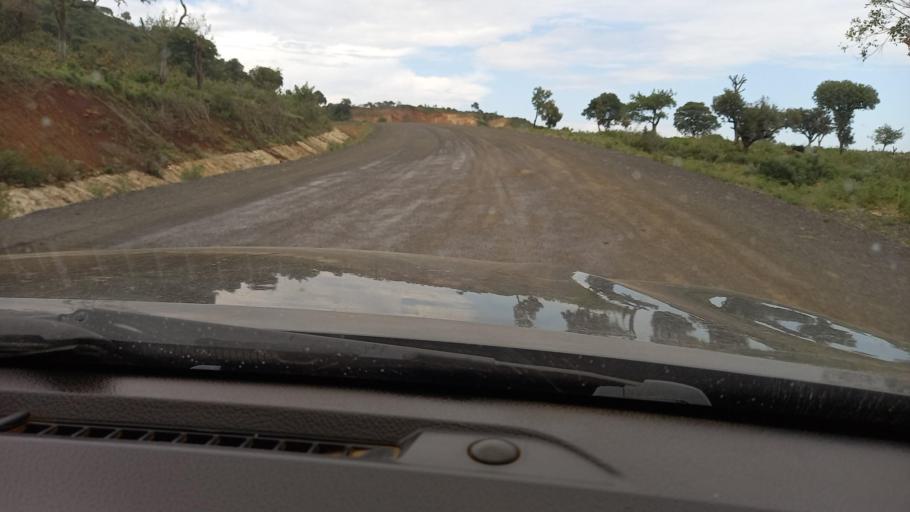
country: ET
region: Southern Nations, Nationalities, and People's Region
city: Mizan Teferi
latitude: 6.2045
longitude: 35.6526
